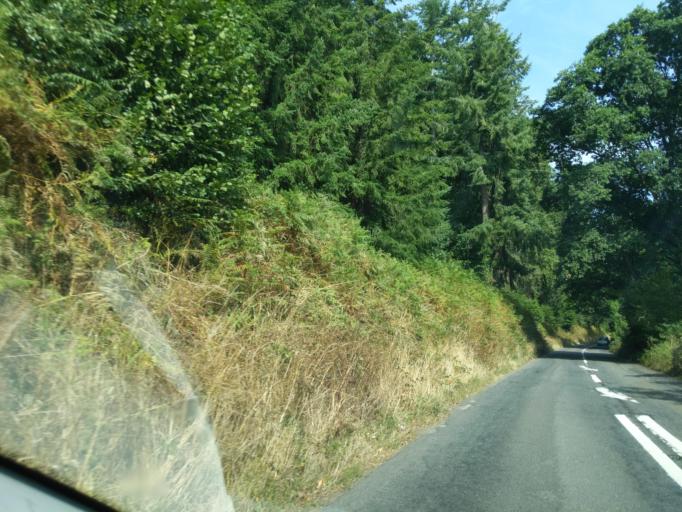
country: GB
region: England
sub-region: Devon
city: Winkleigh
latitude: 50.8876
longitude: -3.8710
